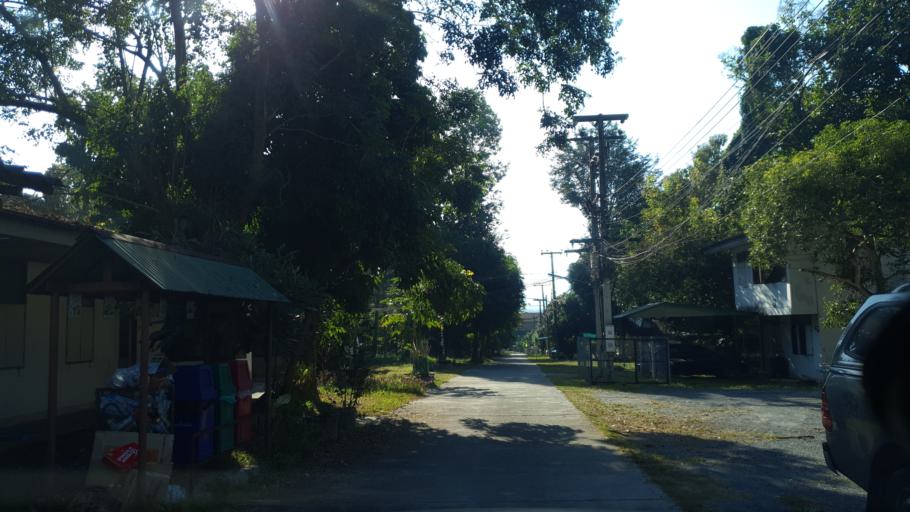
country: TH
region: Chiang Mai
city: Mae On
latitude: 18.7447
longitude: 99.2204
